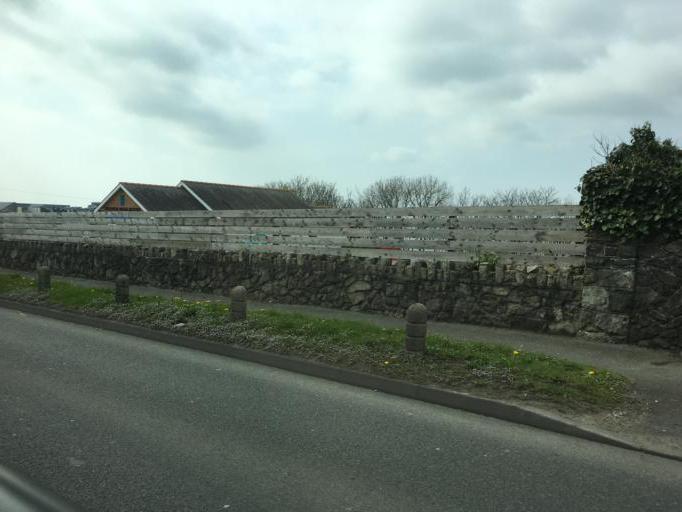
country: GB
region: Wales
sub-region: Gwynedd
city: Caernarfon
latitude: 53.1465
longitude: -4.2689
